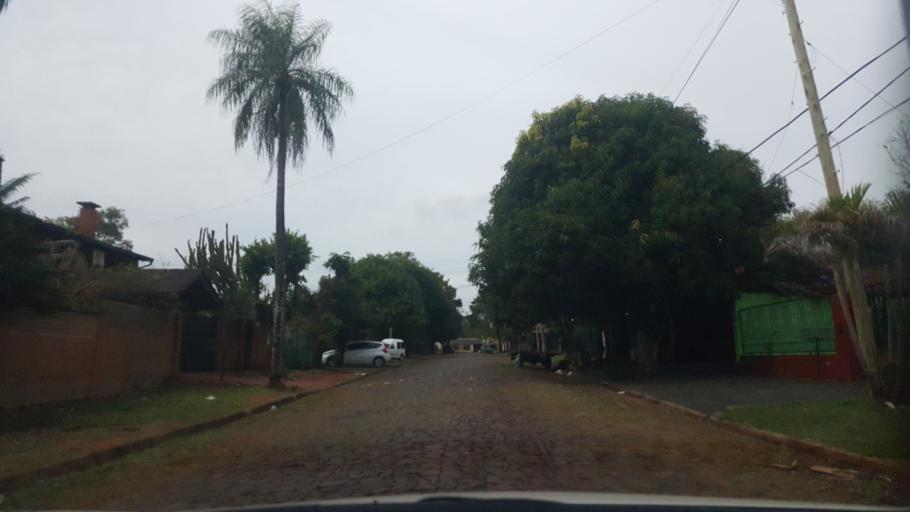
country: AR
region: Misiones
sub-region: Departamento de Capital
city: Posadas
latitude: -27.3846
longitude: -55.9204
